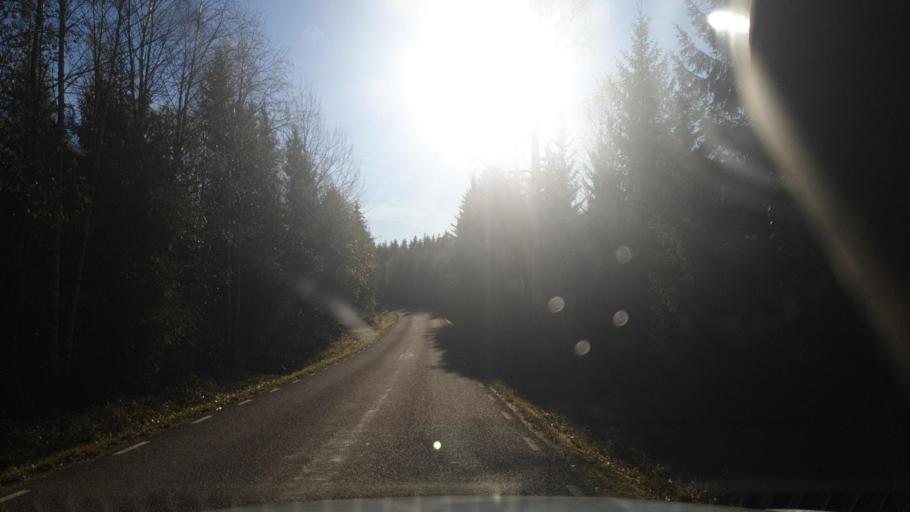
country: SE
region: Vaermland
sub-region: Karlstads Kommun
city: Valberg
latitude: 59.4561
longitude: 13.0843
